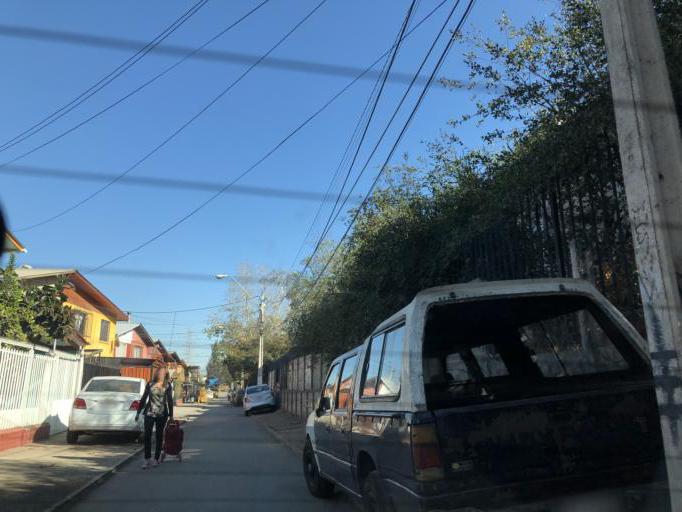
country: CL
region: Santiago Metropolitan
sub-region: Provincia de Santiago
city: La Pintana
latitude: -33.6292
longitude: -70.6232
